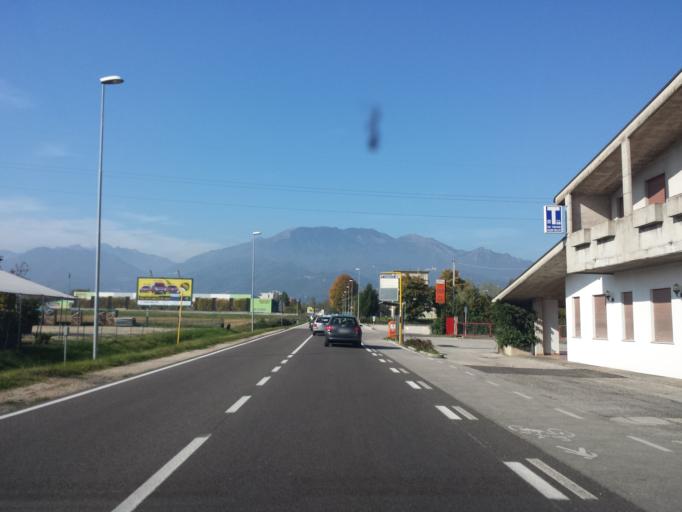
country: IT
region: Veneto
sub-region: Provincia di Vicenza
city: San Vito di Leguzzano
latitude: 45.6978
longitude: 11.3843
